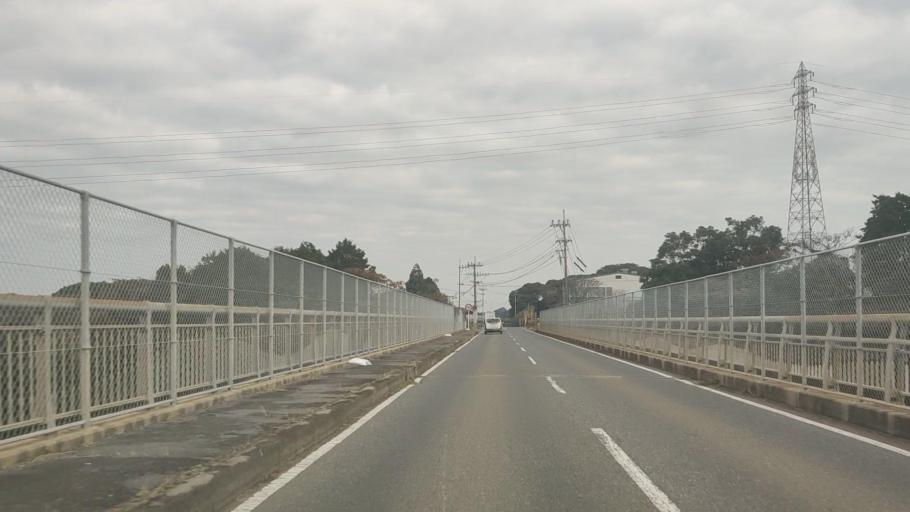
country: JP
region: Nagasaki
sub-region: Isahaya-shi
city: Isahaya
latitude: 32.8076
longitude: 130.1694
